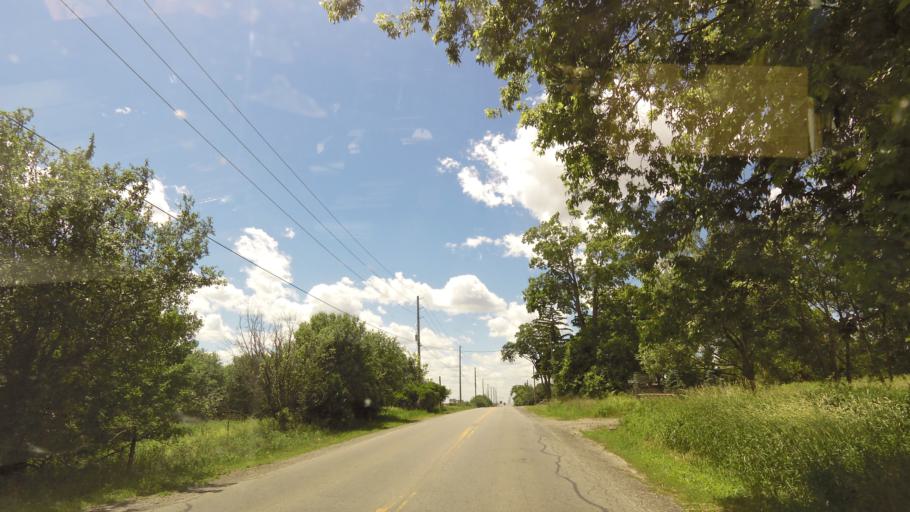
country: CA
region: Ontario
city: Oshawa
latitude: 43.9584
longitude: -78.8502
